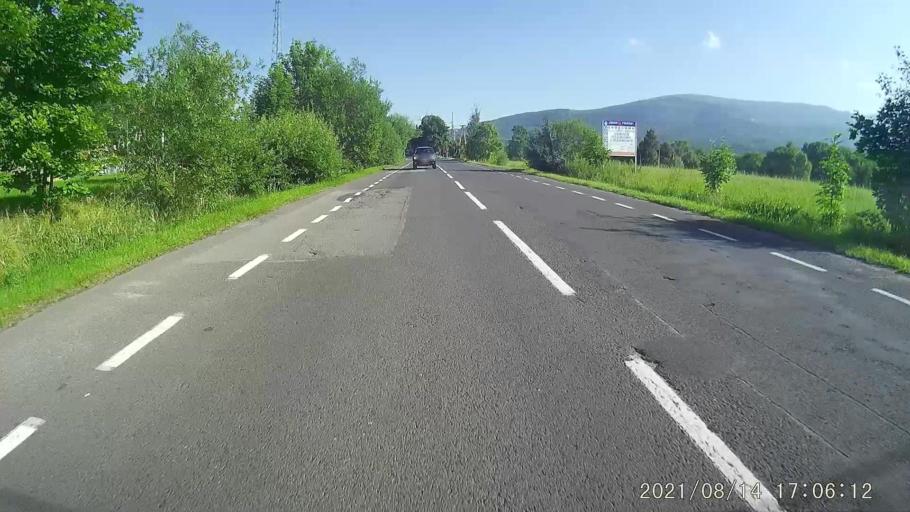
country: PL
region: Lower Silesian Voivodeship
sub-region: Powiat jeleniogorski
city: Kowary
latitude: 50.8083
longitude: 15.8164
